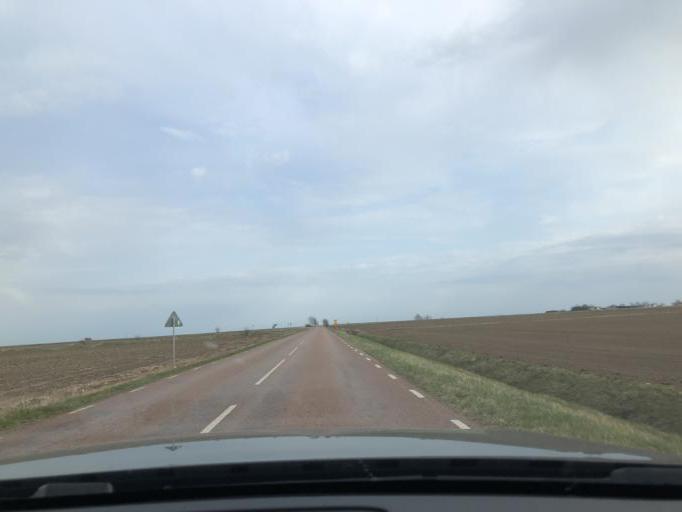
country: SE
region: Kalmar
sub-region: Morbylanga Kommun
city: Moerbylanga
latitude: 56.2861
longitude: 16.4910
